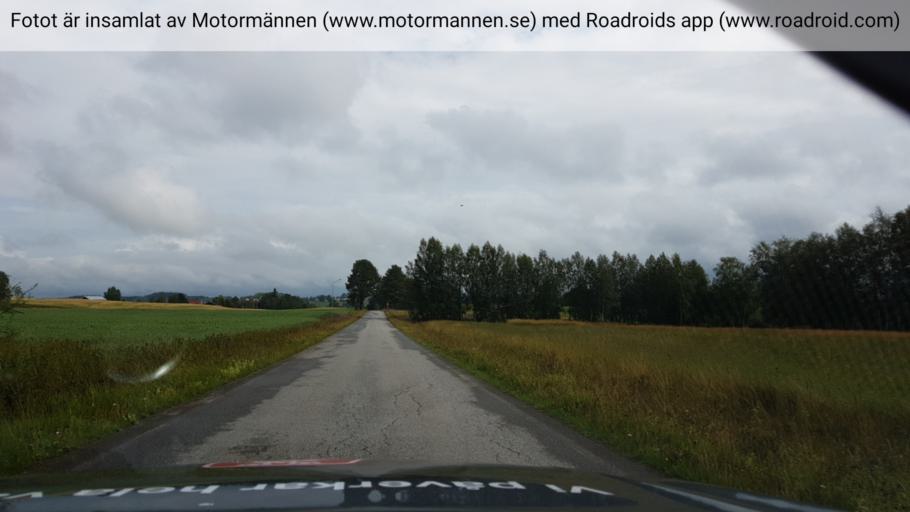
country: SE
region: Jaemtland
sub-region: Krokoms Kommun
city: Krokom
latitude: 63.2933
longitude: 14.4480
